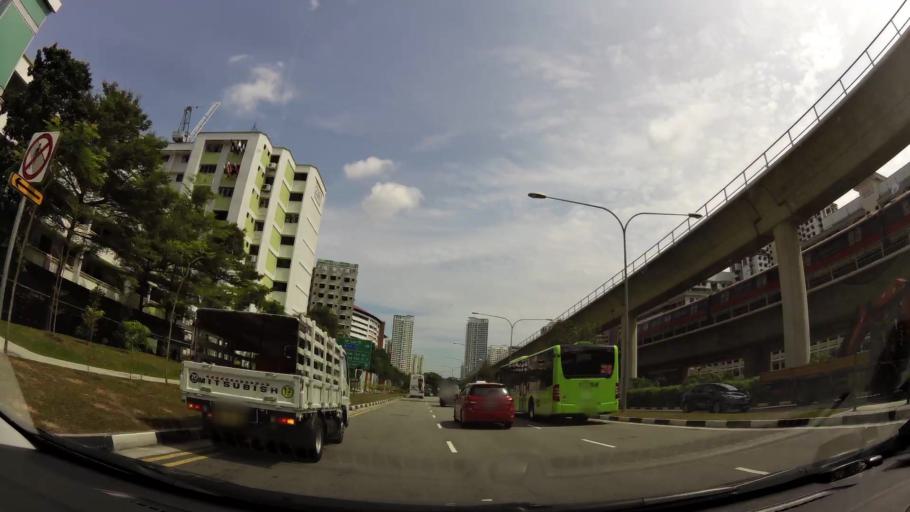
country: SG
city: Singapore
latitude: 1.3398
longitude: 103.7423
